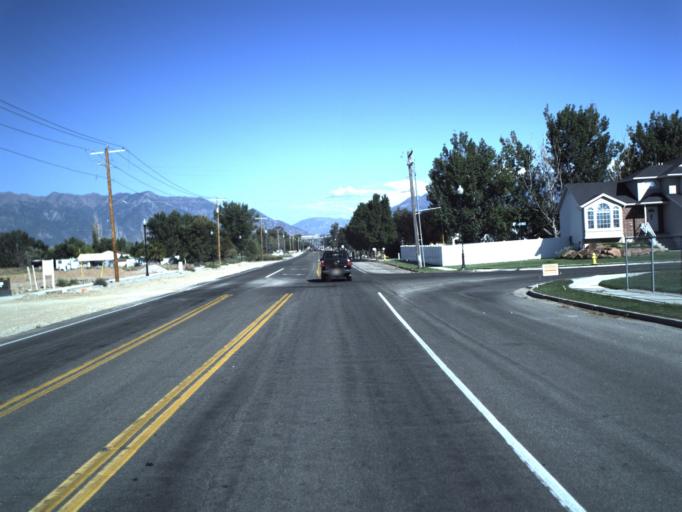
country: US
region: Utah
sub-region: Davis County
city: West Point
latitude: 41.1398
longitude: -112.0925
